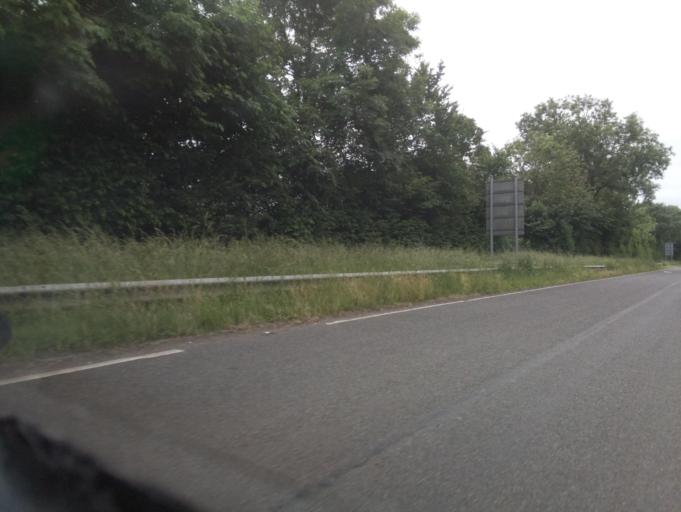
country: GB
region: England
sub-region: Leicestershire
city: Kegworth
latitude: 52.8201
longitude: -1.2697
